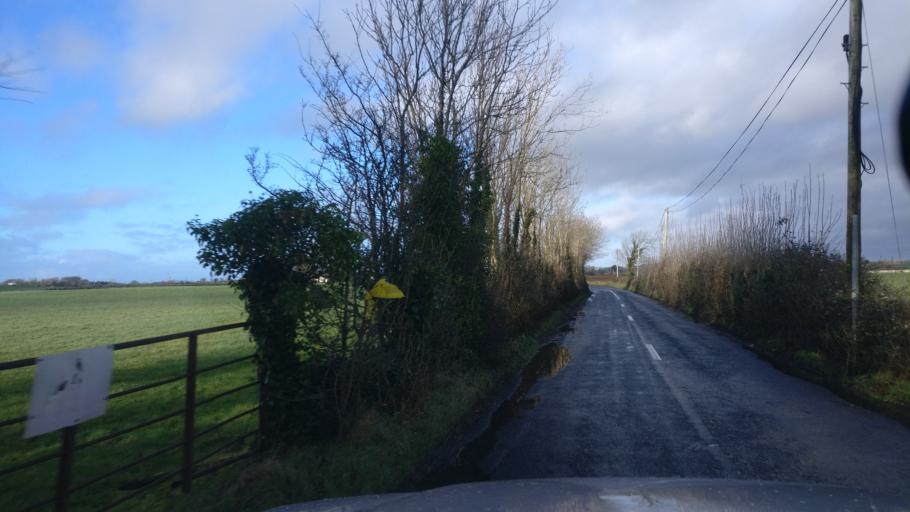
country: IE
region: Connaught
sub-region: County Galway
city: Athenry
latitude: 53.2579
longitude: -8.6795
